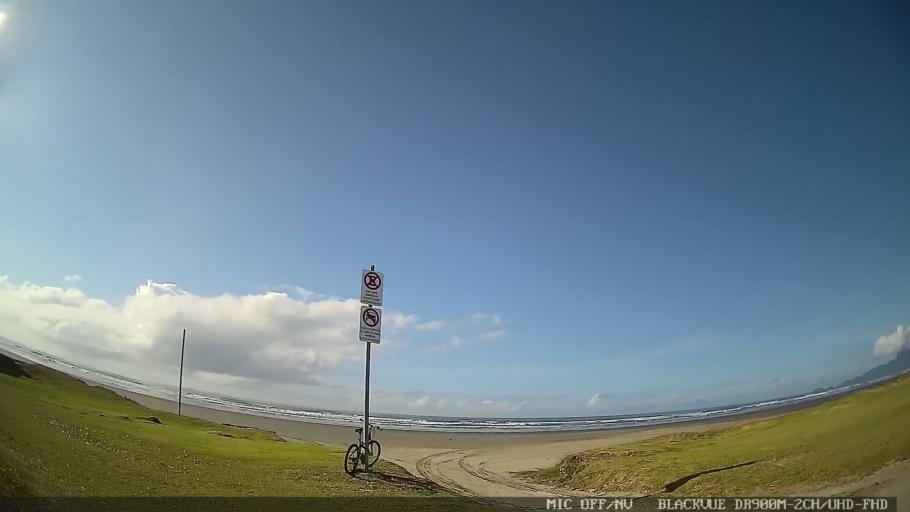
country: BR
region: Sao Paulo
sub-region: Peruibe
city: Peruibe
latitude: -24.2812
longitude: -46.9435
